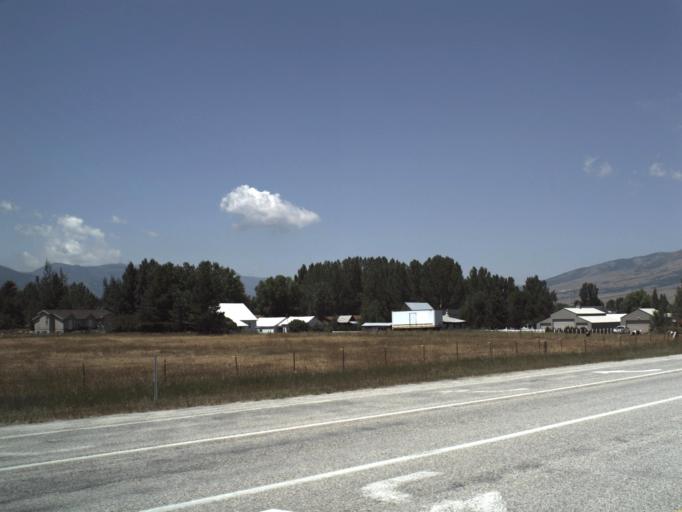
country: US
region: Utah
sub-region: Weber County
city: Wolf Creek
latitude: 41.2532
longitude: -111.7612
